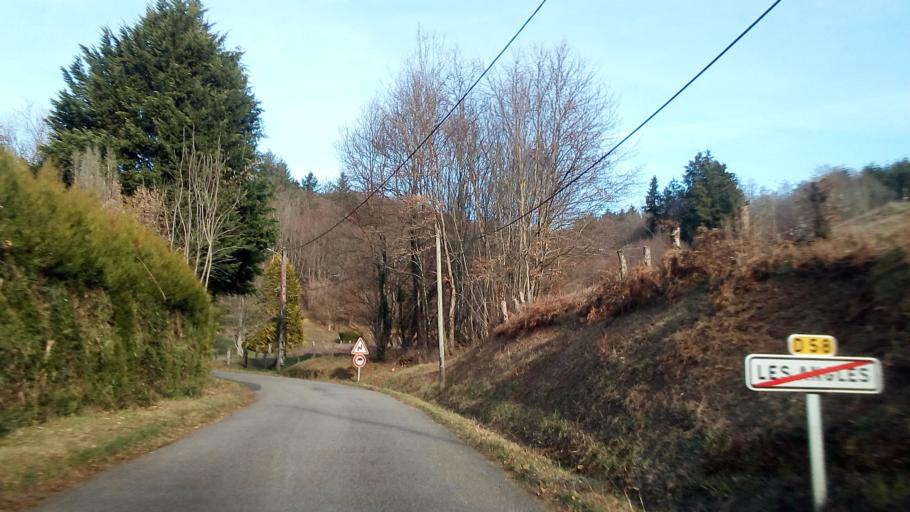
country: FR
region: Limousin
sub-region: Departement de la Correze
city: Naves
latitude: 45.3086
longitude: 1.7952
